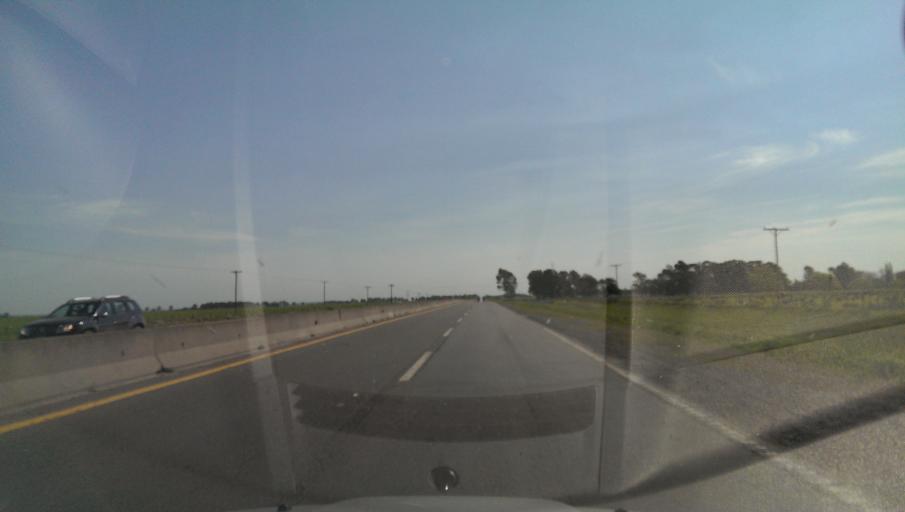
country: AR
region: Buenos Aires
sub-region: Partido de Azul
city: Azul
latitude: -36.8445
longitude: -59.9164
